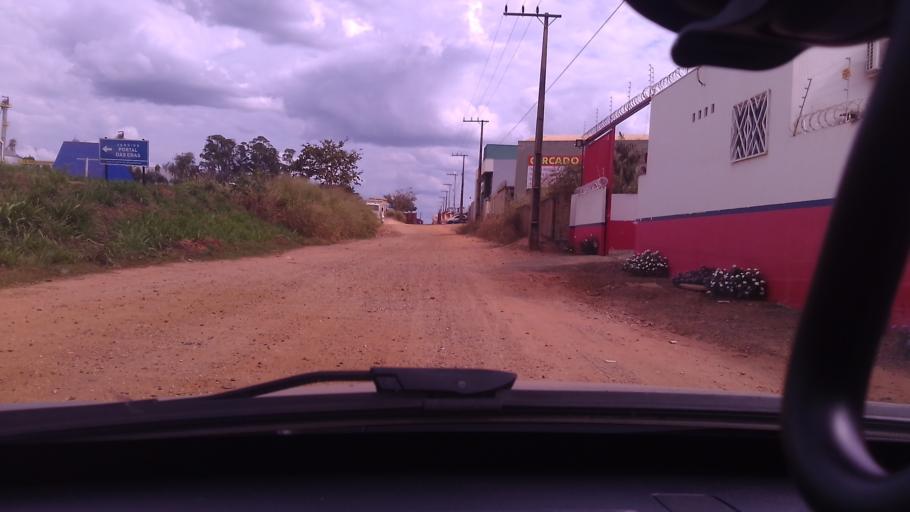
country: BR
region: Goias
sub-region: Mineiros
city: Mineiros
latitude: -17.5806
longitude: -52.5438
